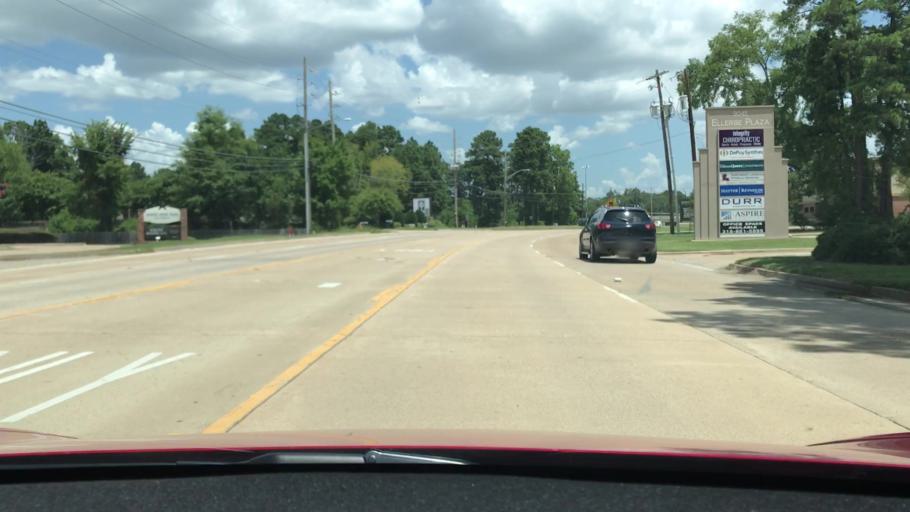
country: US
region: Louisiana
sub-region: Bossier Parish
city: Bossier City
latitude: 32.4122
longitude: -93.7385
